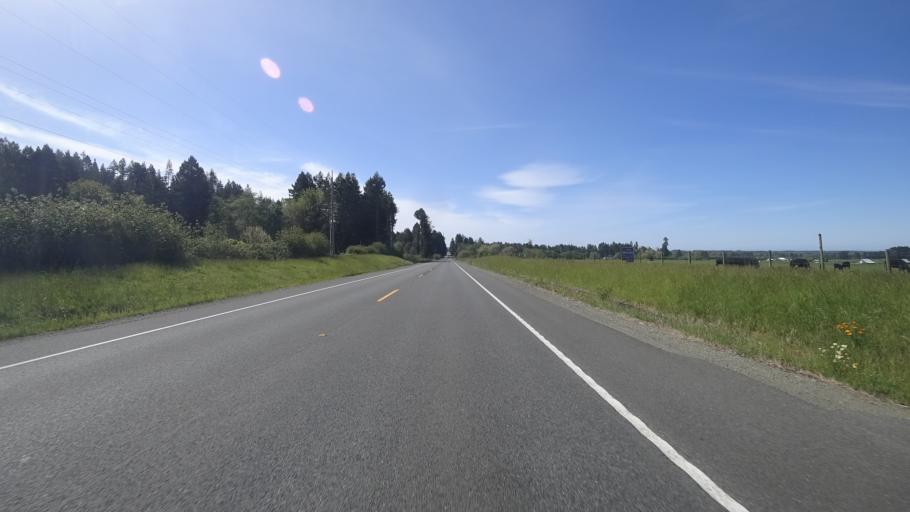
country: US
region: California
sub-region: Del Norte County
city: Bertsch-Oceanview
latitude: 41.9134
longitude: -124.1366
